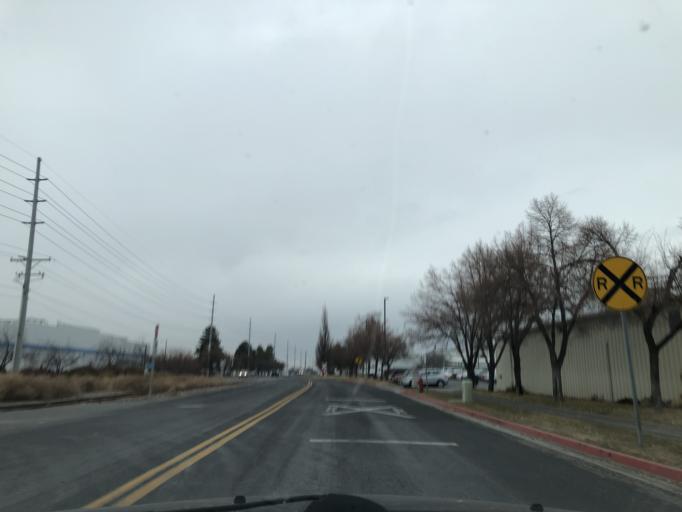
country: US
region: Utah
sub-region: Cache County
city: Logan
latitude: 41.7455
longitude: -111.8492
